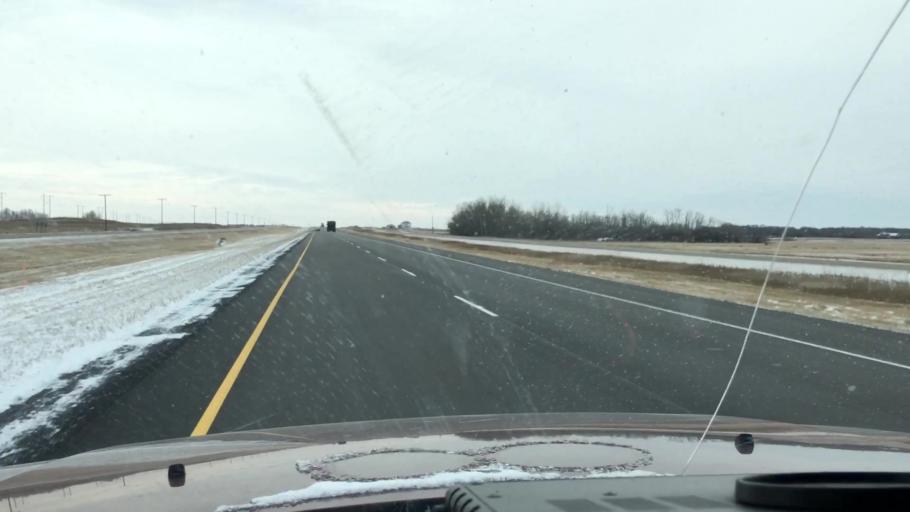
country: CA
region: Saskatchewan
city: Saskatoon
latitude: 51.9372
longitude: -106.5387
